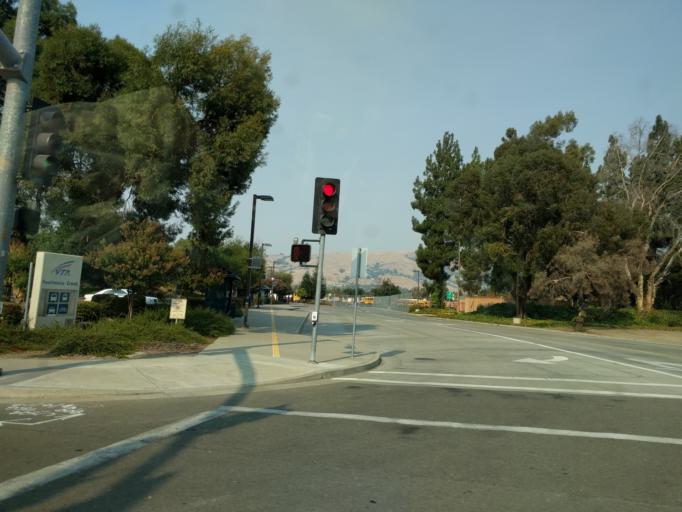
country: US
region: California
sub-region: Santa Clara County
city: Alum Rock
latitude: 37.3819
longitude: -121.8552
